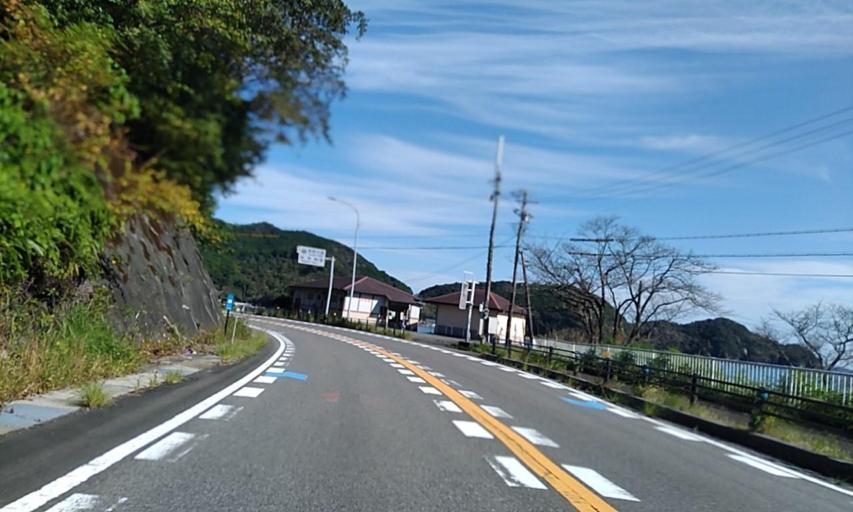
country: JP
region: Mie
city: Owase
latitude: 34.1608
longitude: 136.2767
